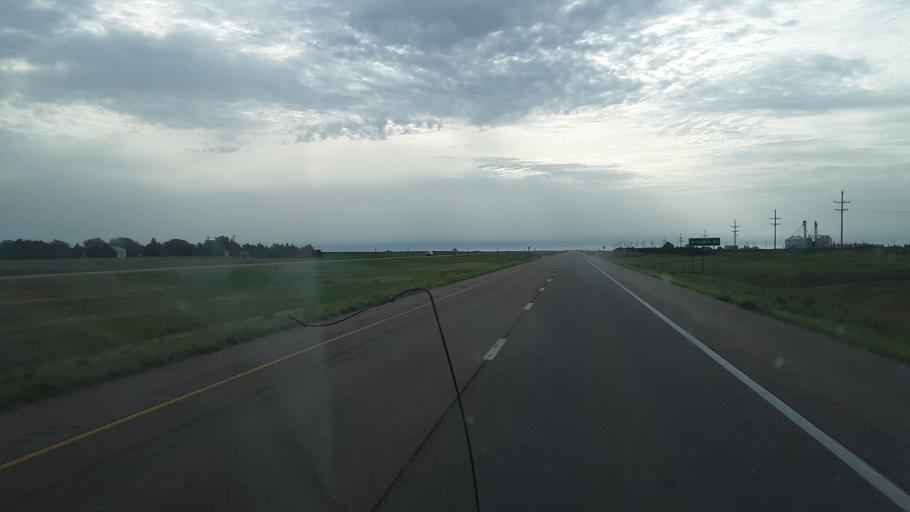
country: US
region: Kansas
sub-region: Finney County
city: Garden City
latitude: 37.9610
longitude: -100.7593
